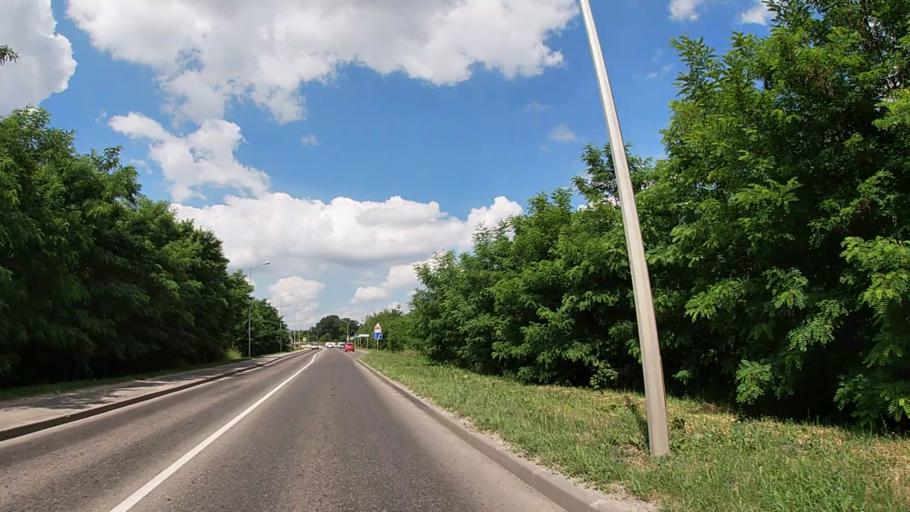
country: RU
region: Belgorod
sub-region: Belgorodskiy Rayon
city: Belgorod
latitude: 50.5946
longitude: 36.5552
